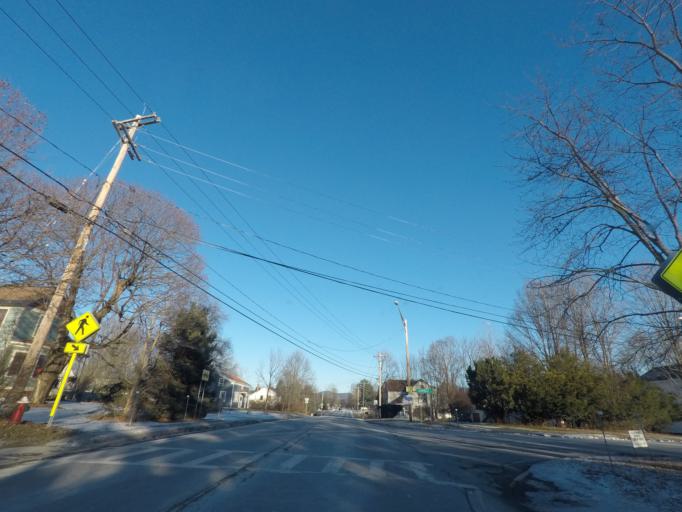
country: US
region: New York
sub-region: Rensselaer County
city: Poestenkill
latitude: 42.7292
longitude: -73.6005
